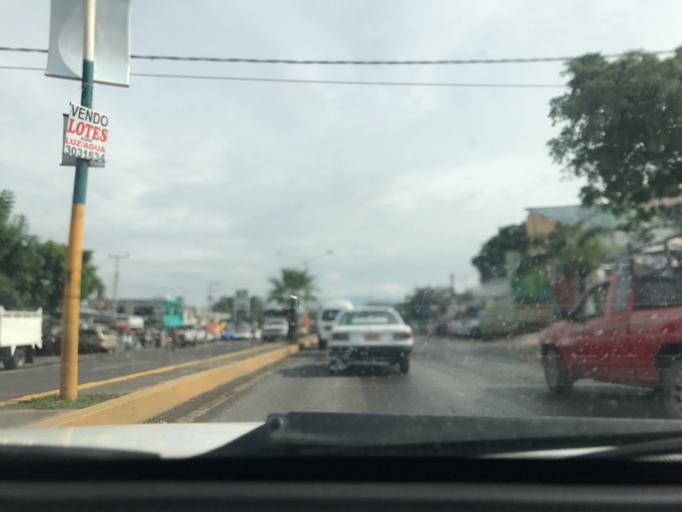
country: MX
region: Morelos
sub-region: Cuautla
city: Tierra Larga (Campo Nuevo)
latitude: 18.8541
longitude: -98.9364
